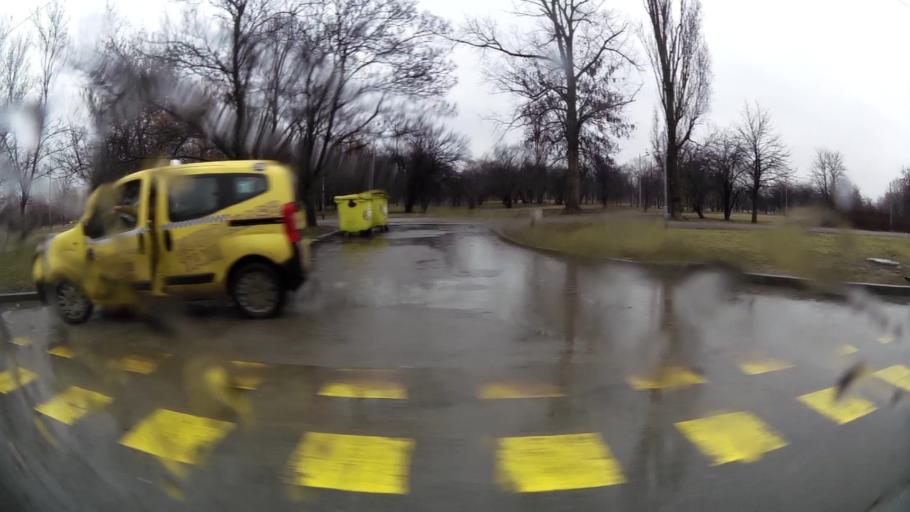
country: BG
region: Sofia-Capital
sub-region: Stolichna Obshtina
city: Sofia
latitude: 42.6554
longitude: 23.3495
